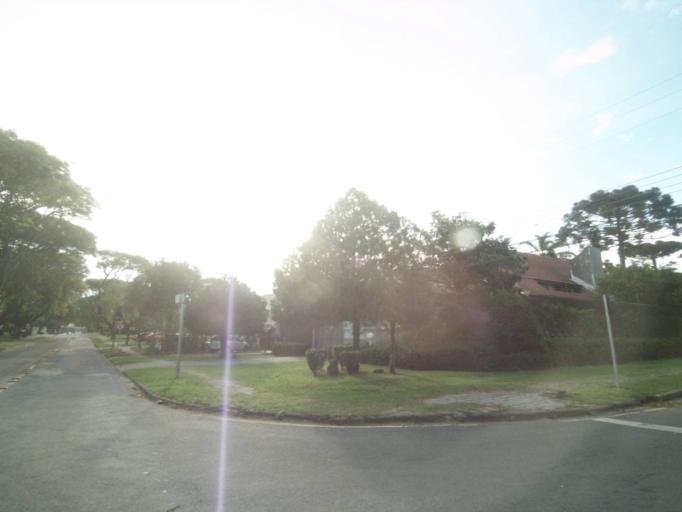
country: BR
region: Parana
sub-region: Curitiba
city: Curitiba
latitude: -25.4257
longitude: -49.2357
